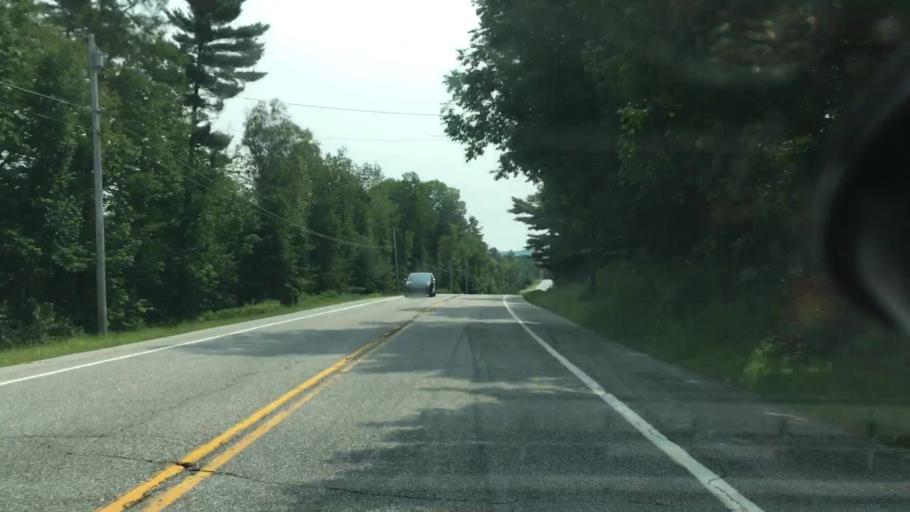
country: US
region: Maine
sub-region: Kennebec County
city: Wayne
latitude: 44.3700
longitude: -70.0923
